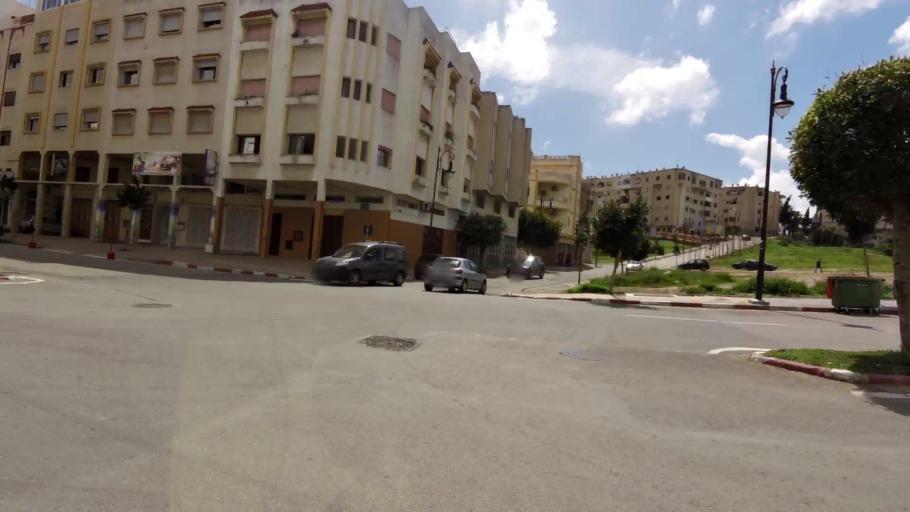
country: MA
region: Tanger-Tetouan
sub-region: Tanger-Assilah
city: Tangier
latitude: 35.7517
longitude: -5.8330
